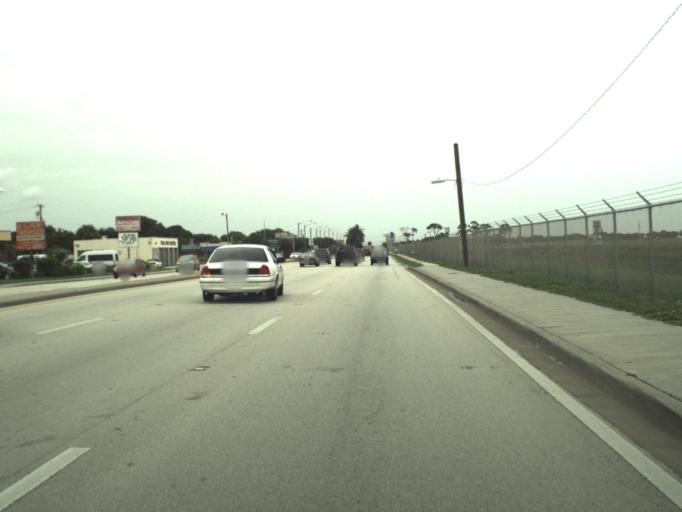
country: US
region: Florida
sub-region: Palm Beach County
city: Haverhill
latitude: 26.6813
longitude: -80.1119
